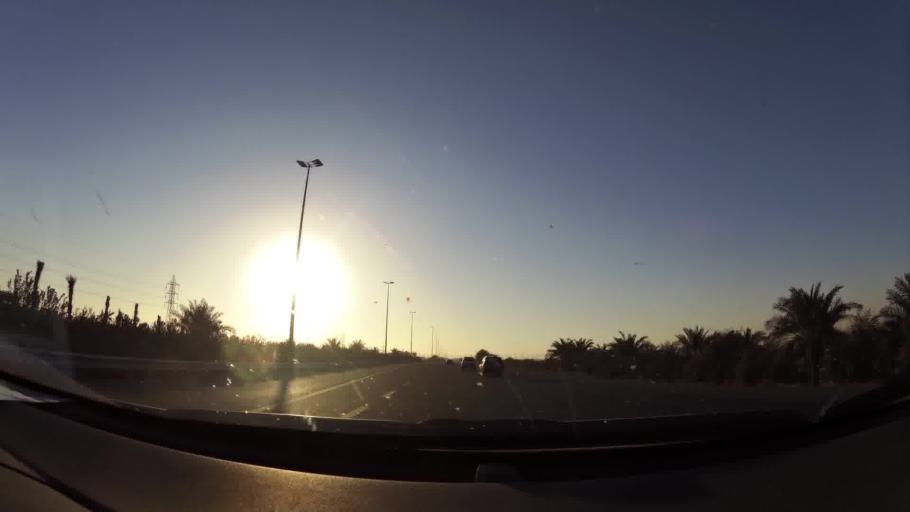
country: KW
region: Al Ahmadi
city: Al Fahahil
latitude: 28.9551
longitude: 48.1718
